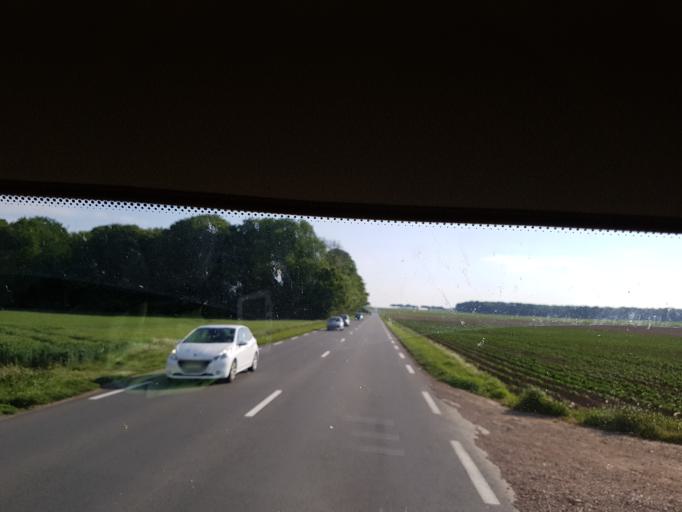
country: FR
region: Picardie
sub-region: Departement de la Somme
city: Crecy-en-Ponthieu
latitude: 50.2187
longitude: 1.9187
